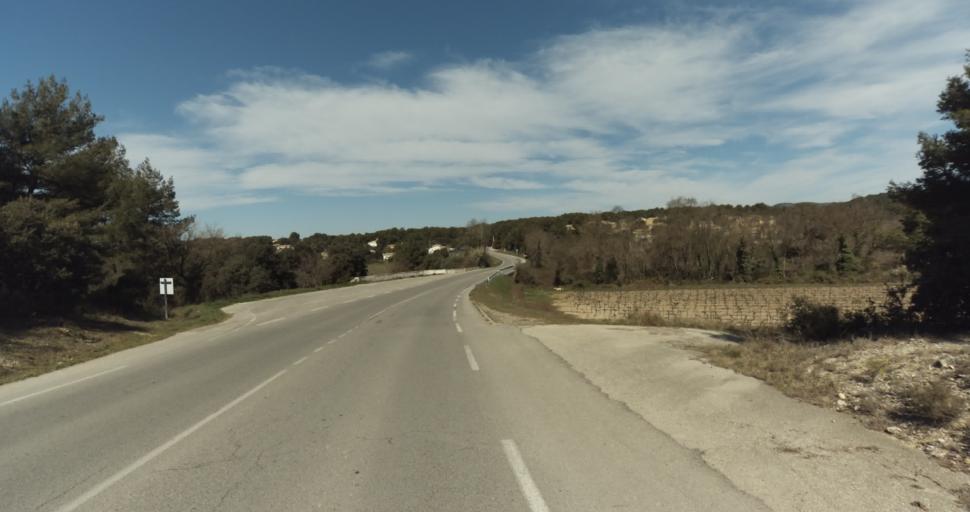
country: FR
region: Provence-Alpes-Cote d'Azur
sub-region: Departement des Bouches-du-Rhone
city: Lambesc
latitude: 43.6411
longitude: 5.2739
